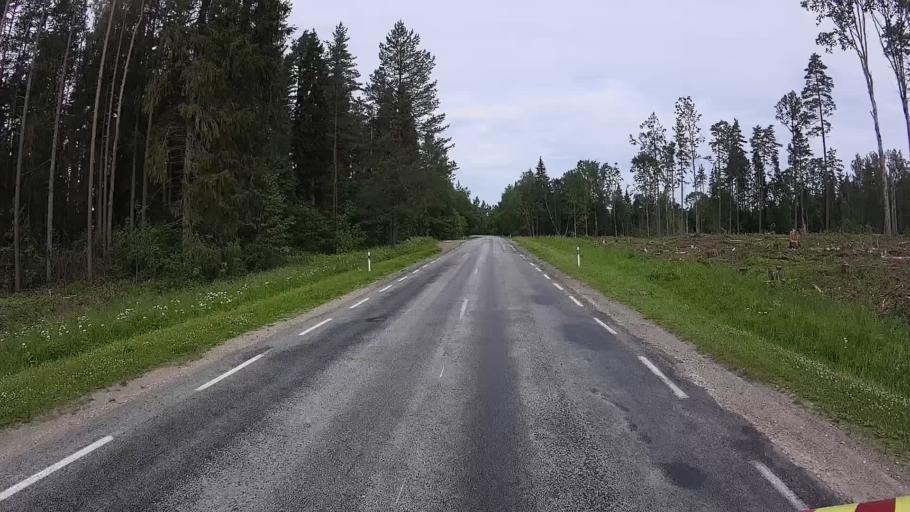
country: EE
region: Viljandimaa
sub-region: Karksi vald
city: Karksi-Nuia
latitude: 58.2212
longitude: 25.6163
